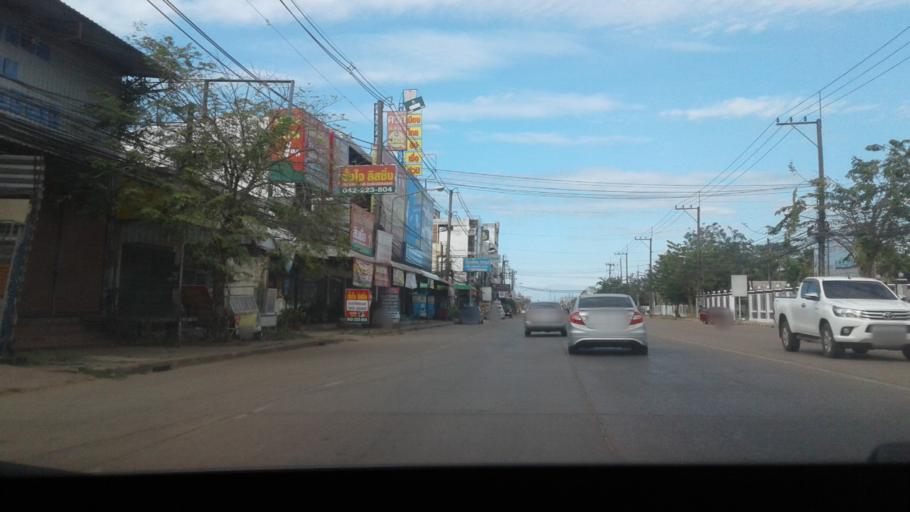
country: TH
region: Changwat Udon Thani
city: Udon Thani
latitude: 17.4262
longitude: 102.7908
